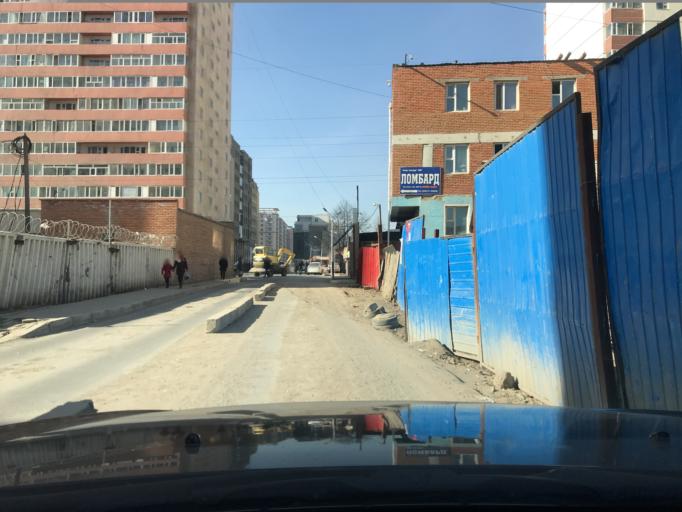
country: MN
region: Ulaanbaatar
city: Ulaanbaatar
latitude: 47.9129
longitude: 106.9515
